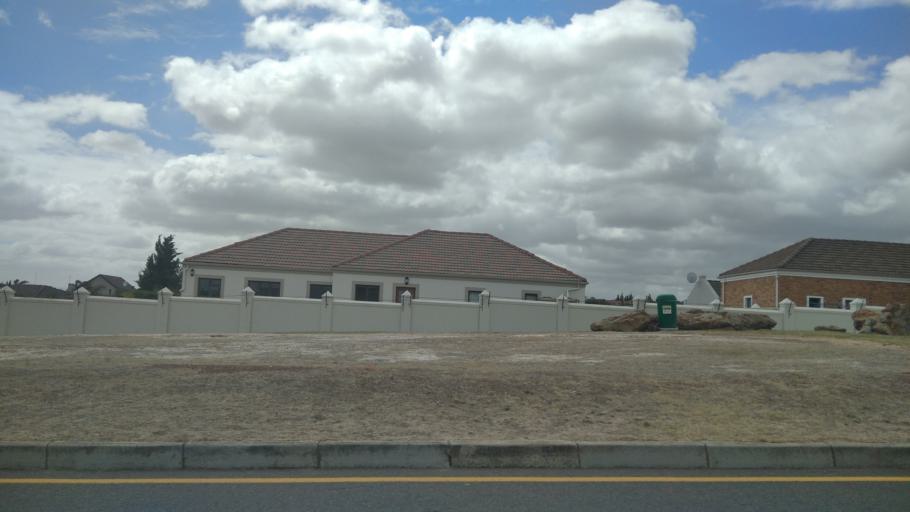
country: ZA
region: Western Cape
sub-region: City of Cape Town
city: Kraaifontein
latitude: -33.8173
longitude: 18.6756
